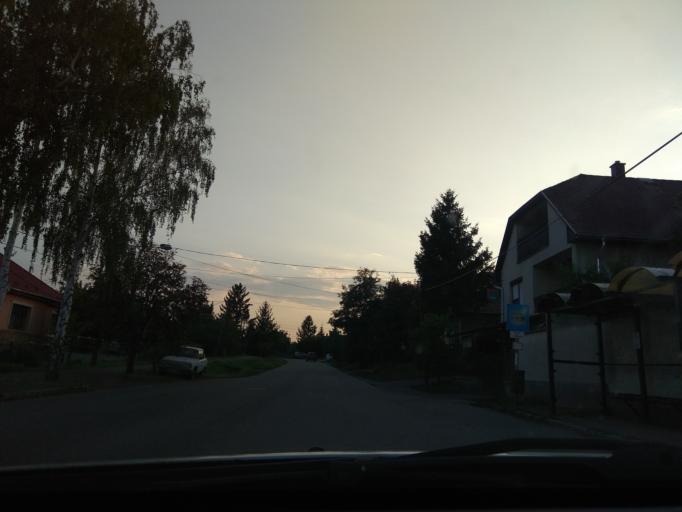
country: HU
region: Borsod-Abauj-Zemplen
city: Szerencs
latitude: 48.1858
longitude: 21.2096
